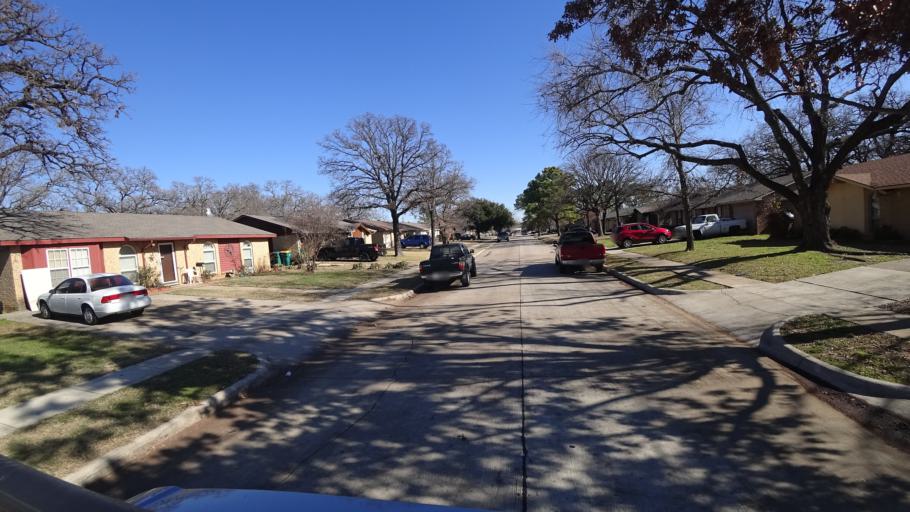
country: US
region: Texas
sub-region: Denton County
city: Lewisville
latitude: 33.0339
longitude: -97.0254
